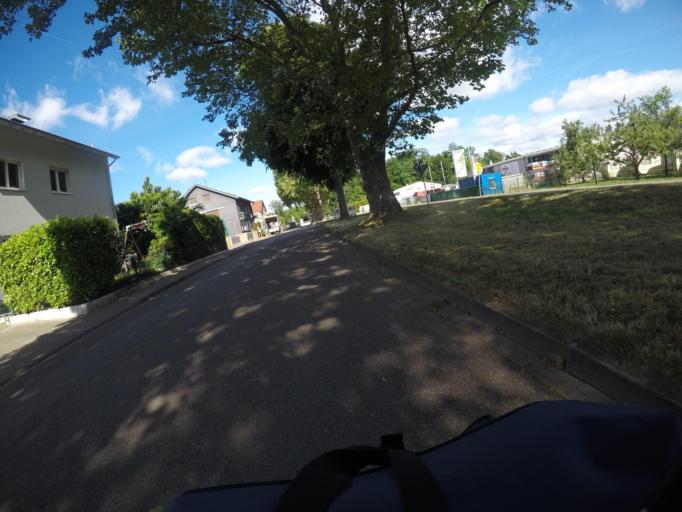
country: DE
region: Baden-Wuerttemberg
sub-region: Karlsruhe Region
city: Durmersheim
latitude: 48.9415
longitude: 8.2521
